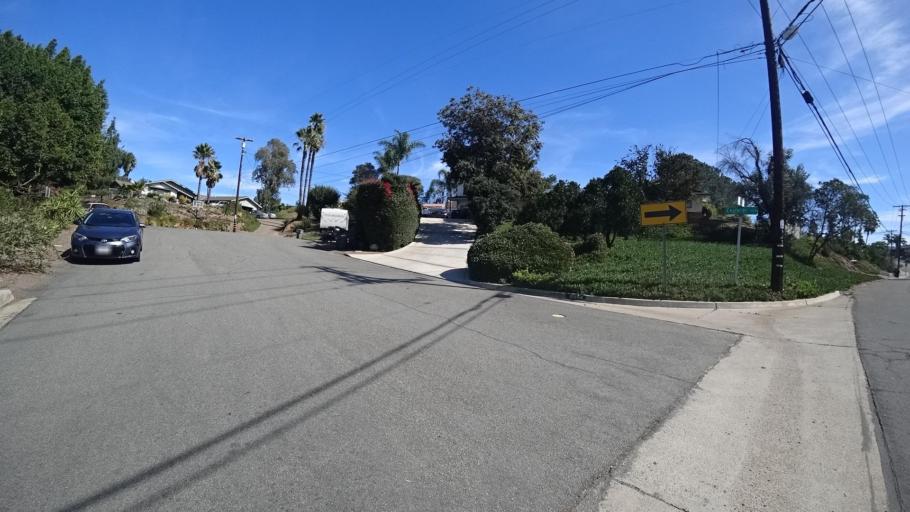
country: US
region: California
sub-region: San Diego County
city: Casa de Oro-Mount Helix
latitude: 32.7578
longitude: -116.9562
